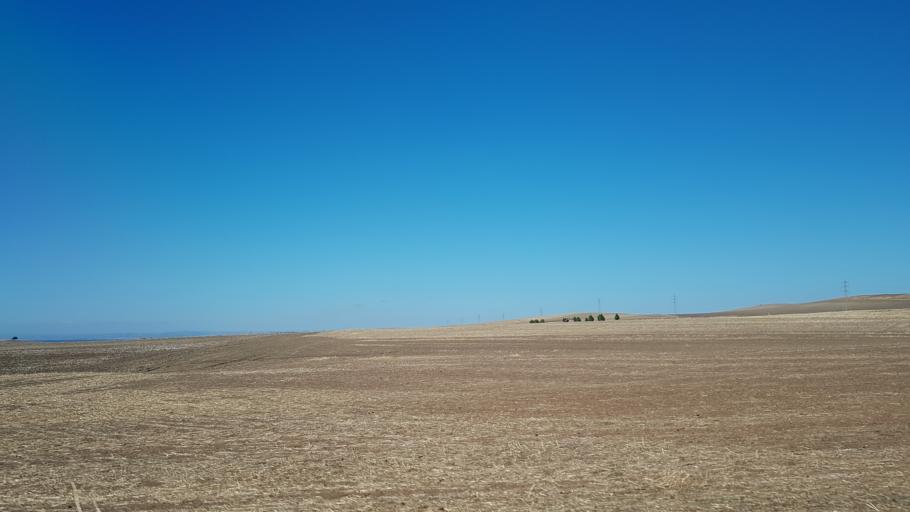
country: TR
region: Tekirdag
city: Corlu
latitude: 41.0209
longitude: 27.8064
